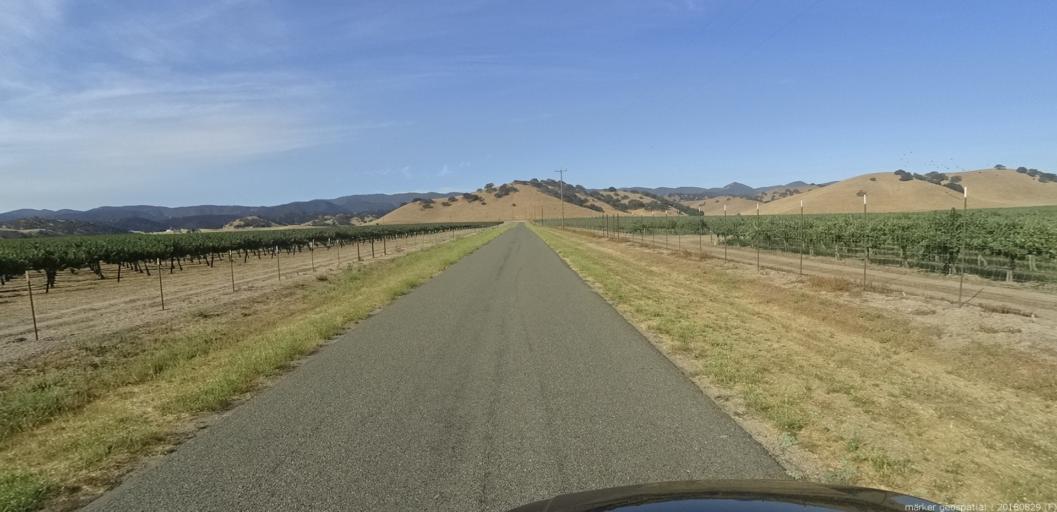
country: US
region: California
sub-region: Monterey County
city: King City
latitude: 36.0847
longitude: -121.0352
